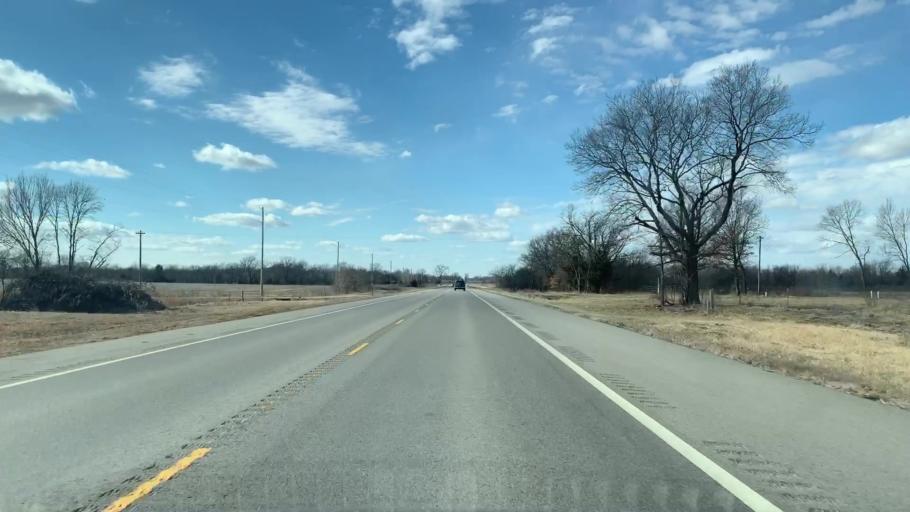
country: US
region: Kansas
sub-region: Labette County
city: Oswego
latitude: 37.3400
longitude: -95.0668
